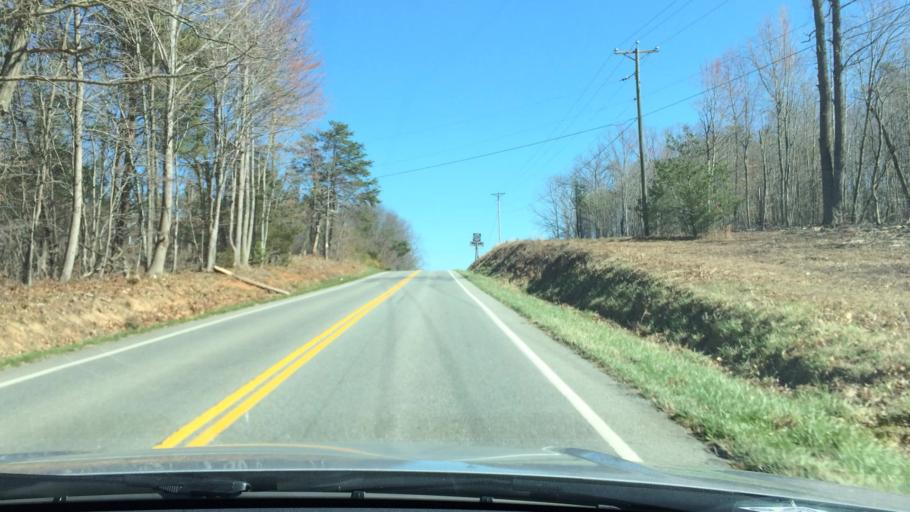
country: US
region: Virginia
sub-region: Franklin County
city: Union Hall
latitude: 36.9882
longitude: -79.6565
